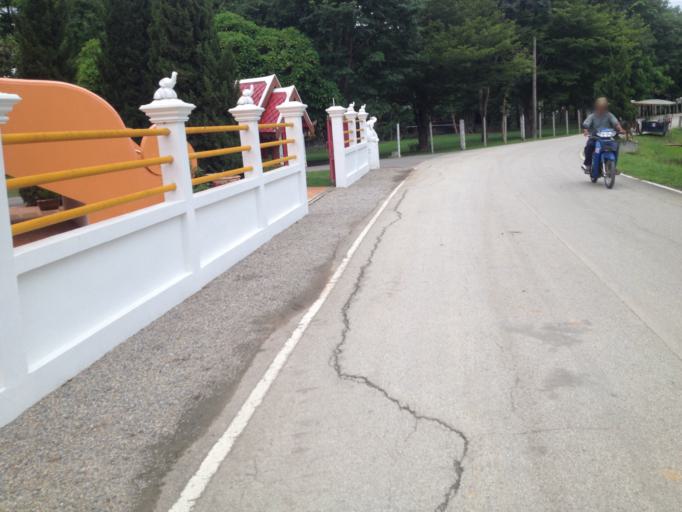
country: TH
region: Chiang Mai
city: Hang Dong
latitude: 18.7087
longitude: 98.9130
